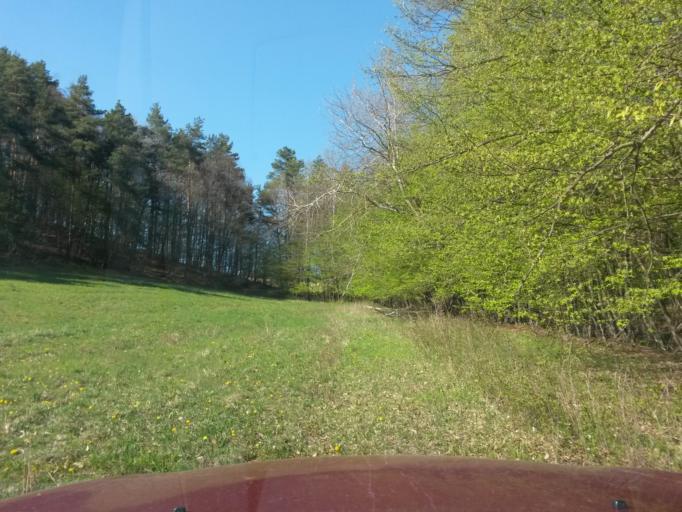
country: SK
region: Presovsky
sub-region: Okres Presov
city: Presov
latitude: 48.9628
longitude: 21.1110
